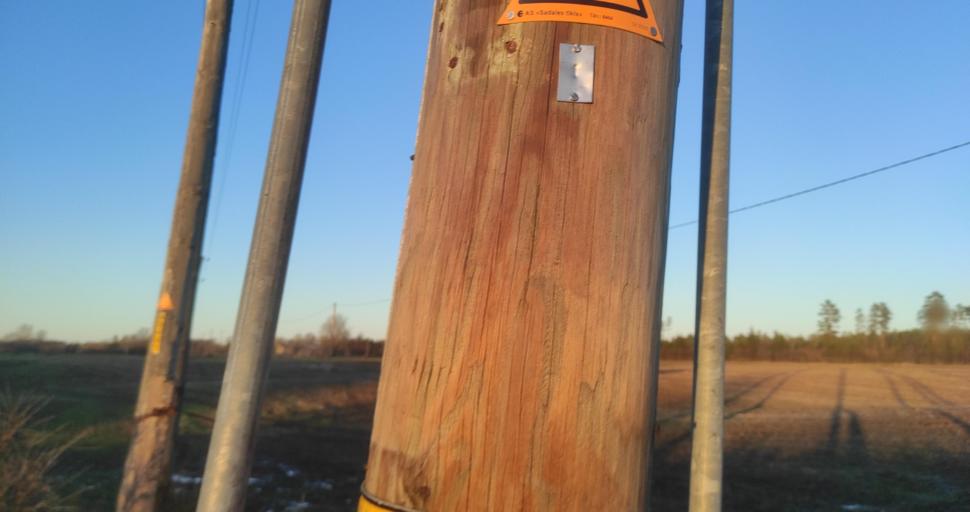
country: LV
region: Dundaga
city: Dundaga
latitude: 57.3867
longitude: 22.0888
